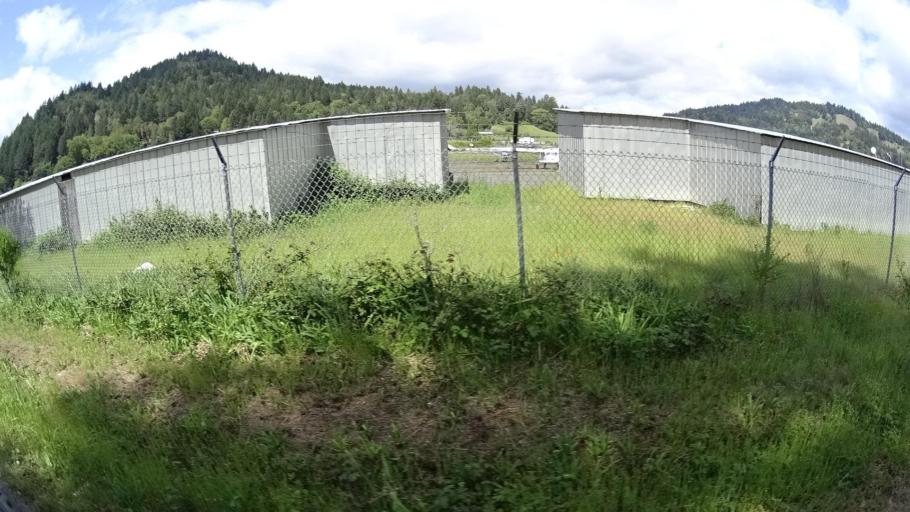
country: US
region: California
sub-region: Humboldt County
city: Redway
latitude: 40.0856
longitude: -123.8125
